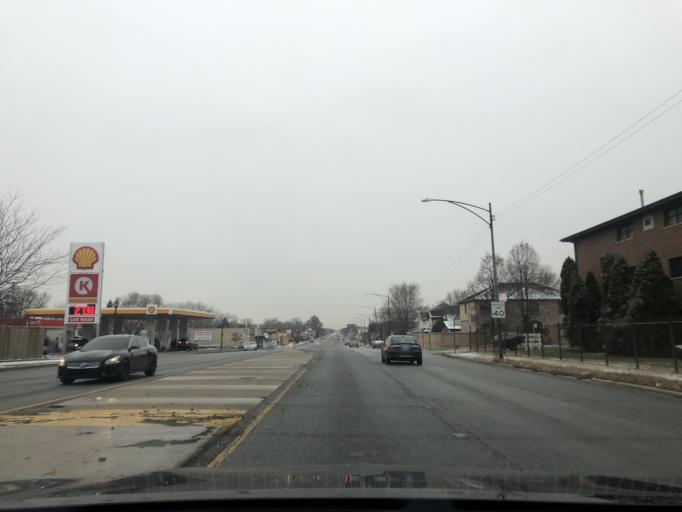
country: US
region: Illinois
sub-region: Cook County
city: Evergreen Park
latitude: 41.7355
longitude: -87.6874
